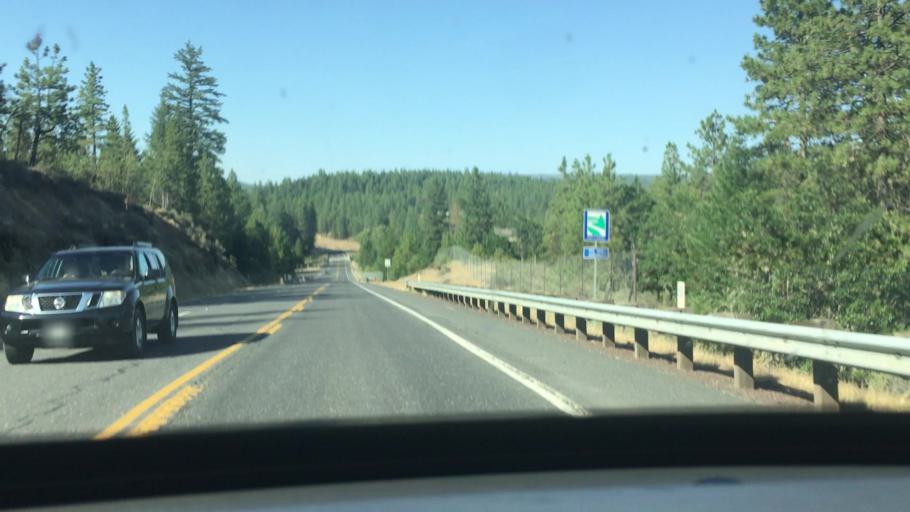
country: US
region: Washington
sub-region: Klickitat County
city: Goldendale
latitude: 45.9100
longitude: -120.7098
